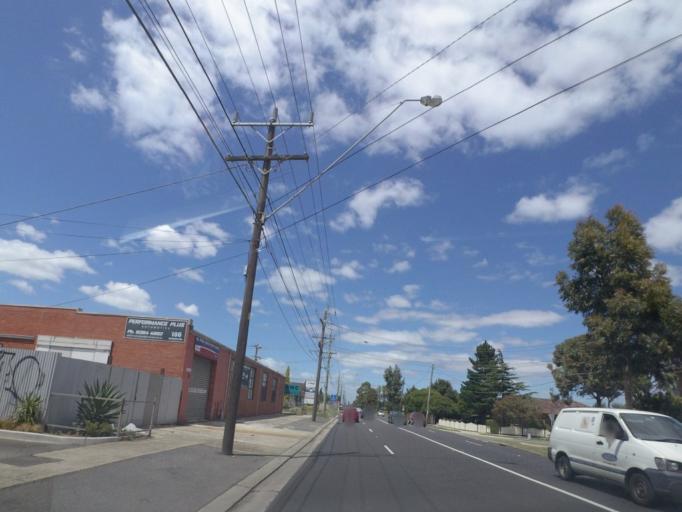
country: AU
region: Victoria
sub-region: Brimbank
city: Albion
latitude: -37.7569
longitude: 144.8325
